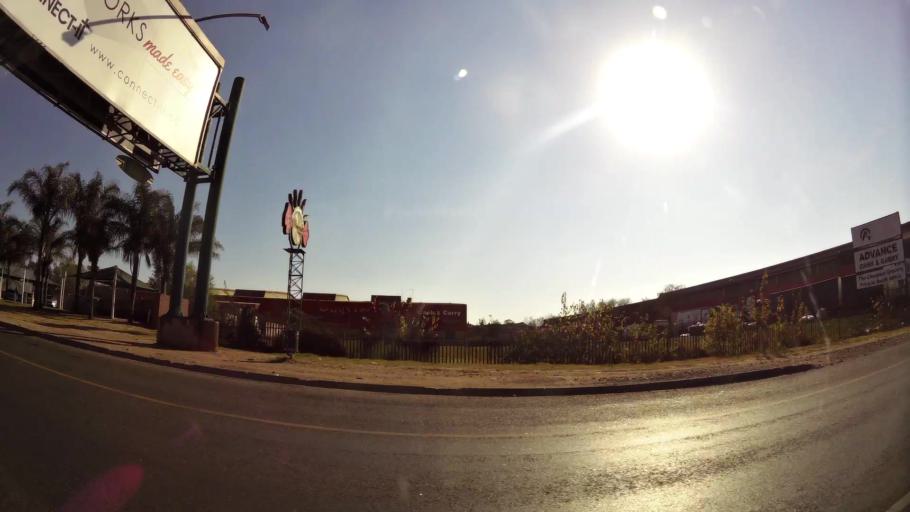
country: ZA
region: Gauteng
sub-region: City of Tshwane Metropolitan Municipality
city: Pretoria
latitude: -25.7154
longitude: 28.1697
